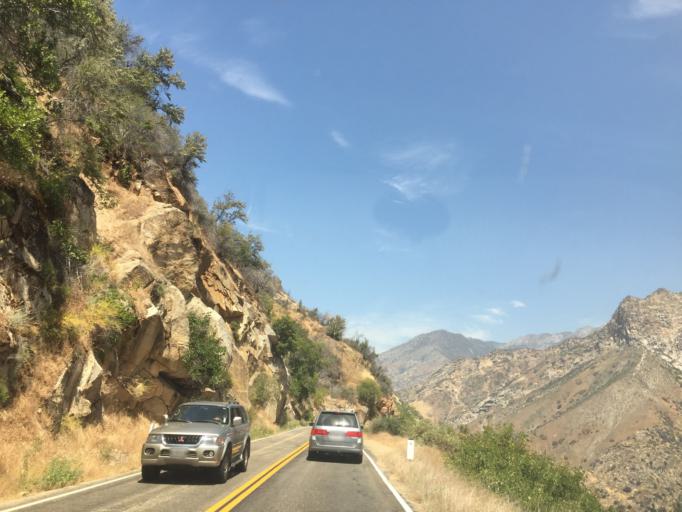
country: US
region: California
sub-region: Tulare County
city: Three Rivers
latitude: 36.8179
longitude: -118.8408
